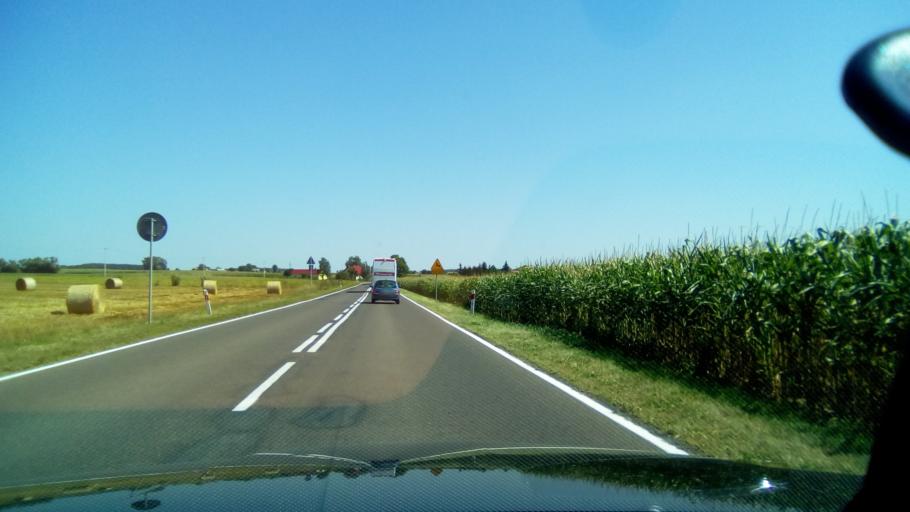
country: PL
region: Masovian Voivodeship
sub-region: Powiat plocki
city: Starozreby
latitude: 52.6447
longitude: 20.0414
